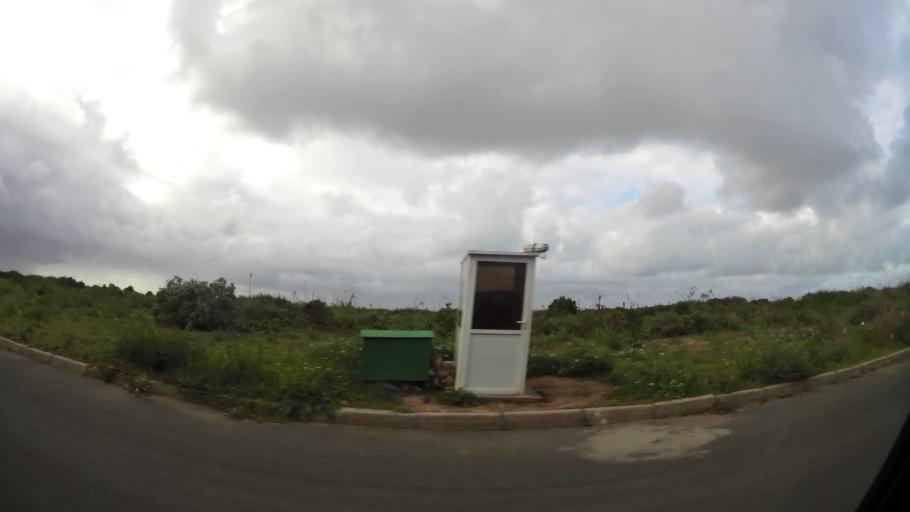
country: MA
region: Grand Casablanca
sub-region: Casablanca
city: Casablanca
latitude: 33.5794
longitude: -7.6965
